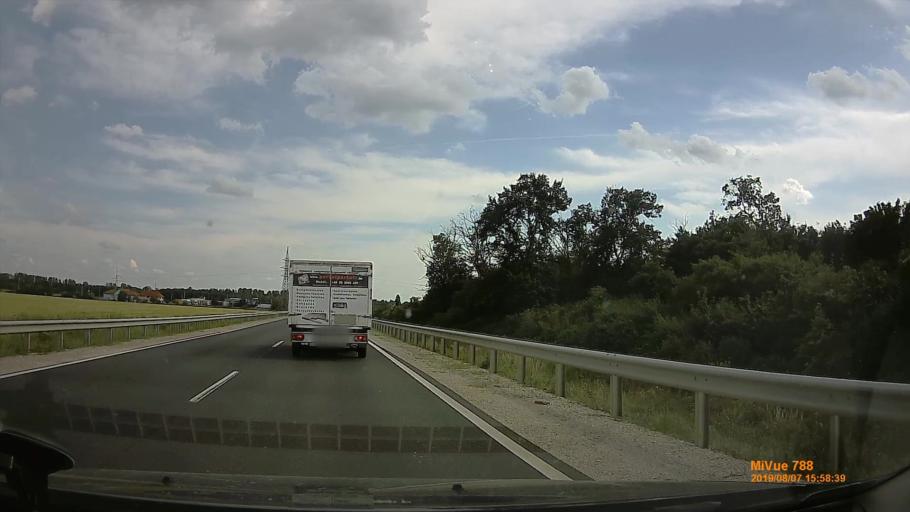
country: HU
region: Vas
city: Kormend
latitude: 47.0243
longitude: 16.6141
